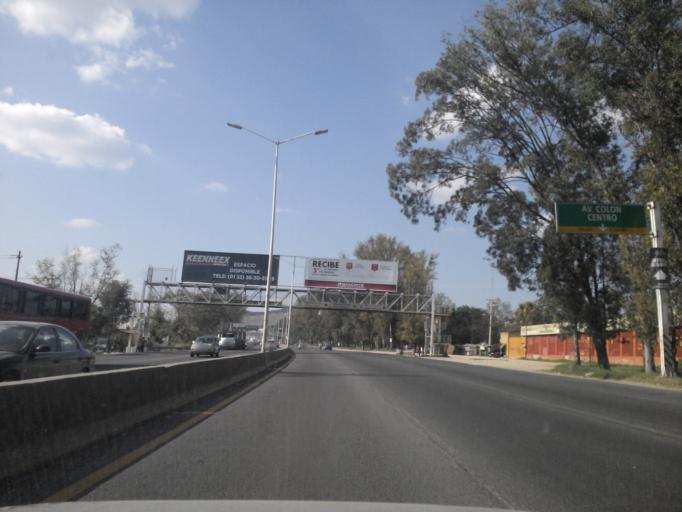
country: MX
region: Jalisco
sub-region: San Pedro Tlaquepaque
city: Paseo del Prado
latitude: 20.5974
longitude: -103.3915
